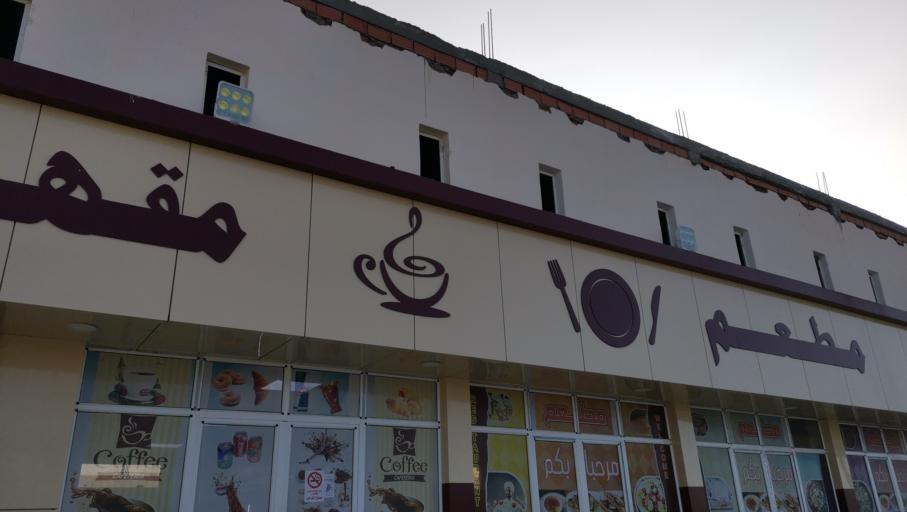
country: DZ
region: Ouargla
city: Hassi Messaoud
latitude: 31.3846
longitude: 6.9095
